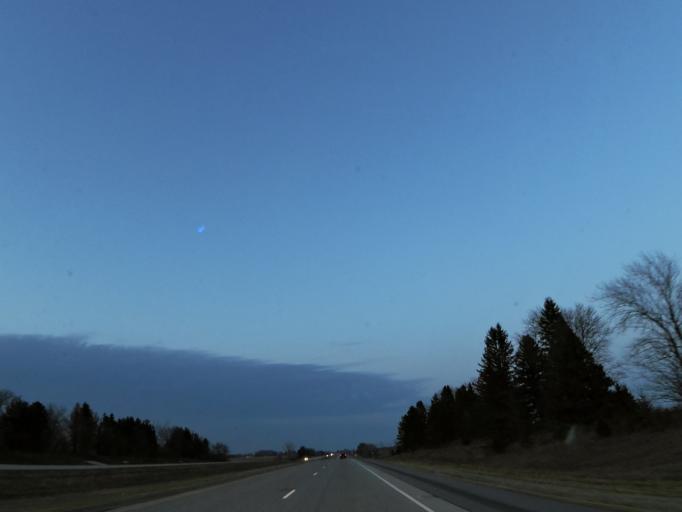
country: US
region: Minnesota
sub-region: Mower County
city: Grand Meadow
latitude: 43.7924
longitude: -92.6043
